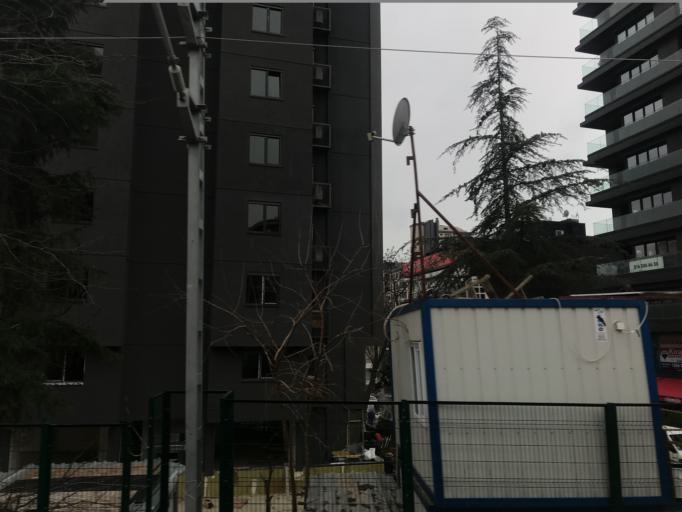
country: TR
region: Istanbul
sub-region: Atasehir
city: Atasehir
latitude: 40.9619
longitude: 29.0793
